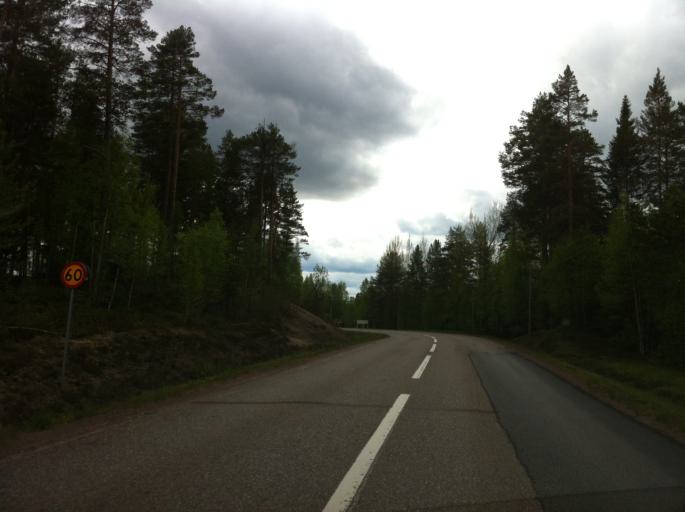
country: NO
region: Hedmark
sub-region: Trysil
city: Innbygda
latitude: 61.4229
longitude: 13.0875
